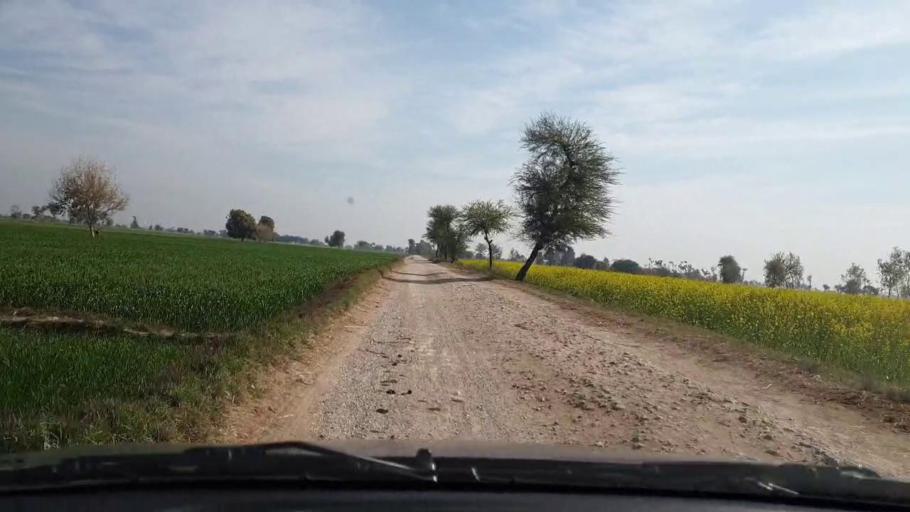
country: PK
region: Sindh
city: Jam Sahib
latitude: 26.2596
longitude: 68.6948
